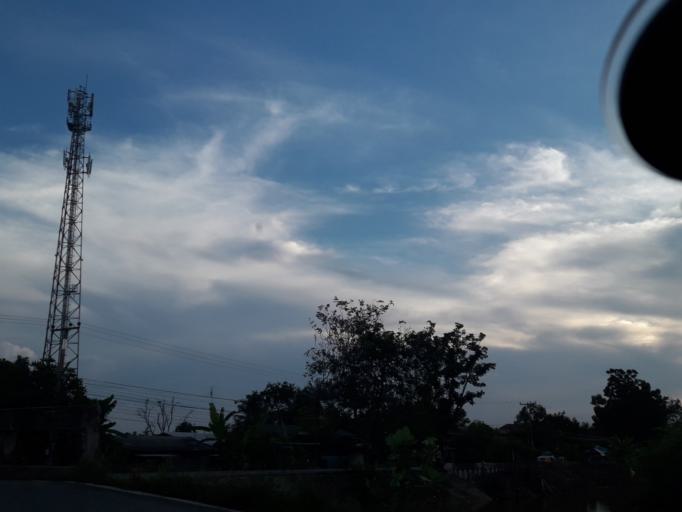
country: TH
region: Sara Buri
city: Nong Khae
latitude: 14.2756
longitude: 100.8905
